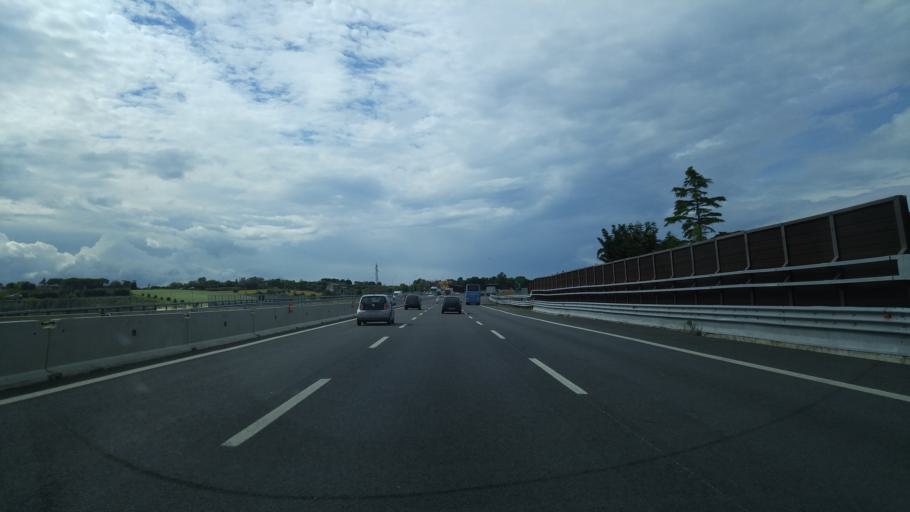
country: IT
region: Emilia-Romagna
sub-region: Provincia di Rimini
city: Rivazzurra
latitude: 44.0141
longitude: 12.5902
